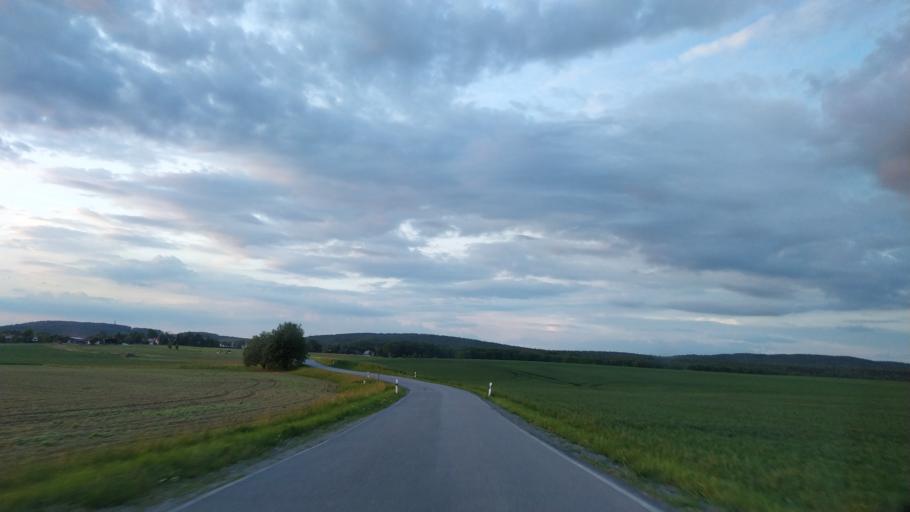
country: DE
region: Saxony
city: Stadt Wehlen
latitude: 50.9765
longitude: 14.0210
